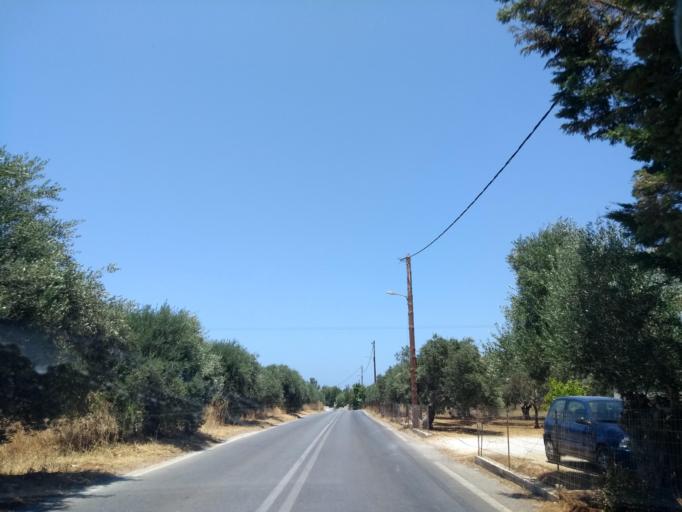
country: GR
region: Crete
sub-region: Nomos Chanias
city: Pithari
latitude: 35.5441
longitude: 24.0824
